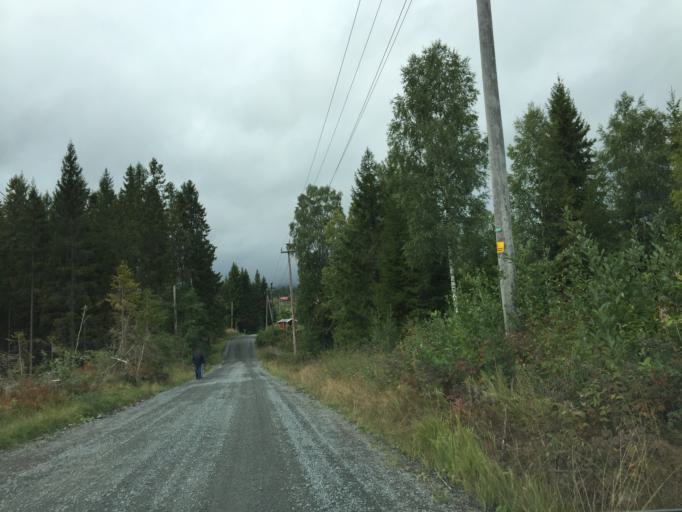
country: NO
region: Akershus
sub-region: Baerum
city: Lysaker
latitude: 60.0194
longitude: 10.5668
